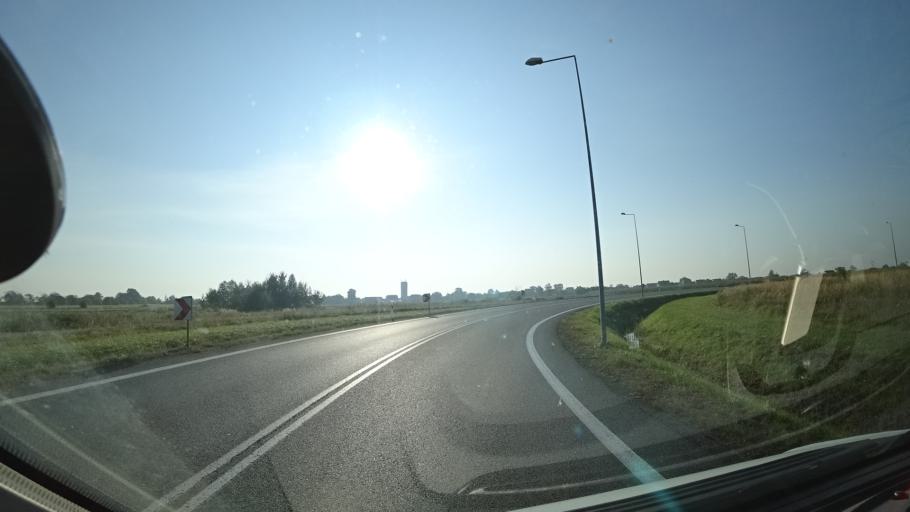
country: PL
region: Silesian Voivodeship
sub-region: Powiat gliwicki
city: Sosnicowice
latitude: 50.2822
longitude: 18.5772
